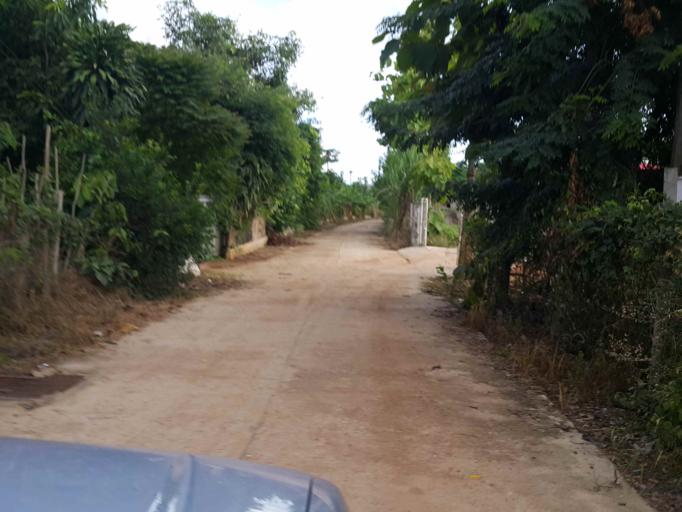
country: TH
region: Chiang Mai
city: Mae Chaem
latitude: 18.4943
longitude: 98.3639
